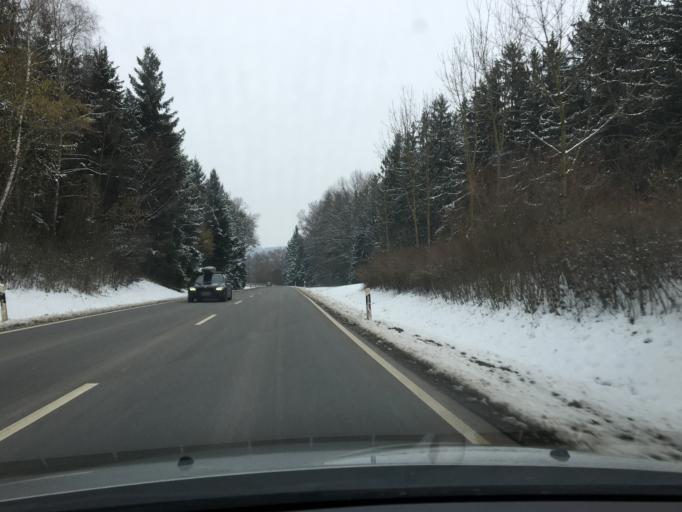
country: DE
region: Bavaria
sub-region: Lower Bavaria
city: Furth
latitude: 48.4354
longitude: 12.3798
